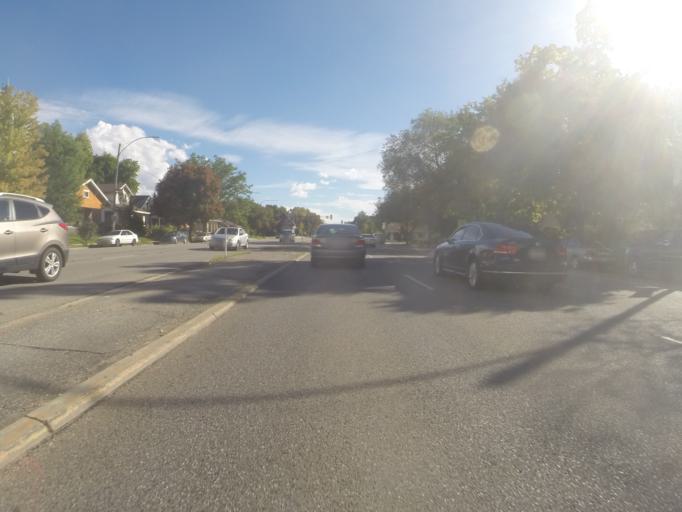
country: US
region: Utah
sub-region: Salt Lake County
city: Salt Lake City
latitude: 40.7511
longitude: -111.8712
